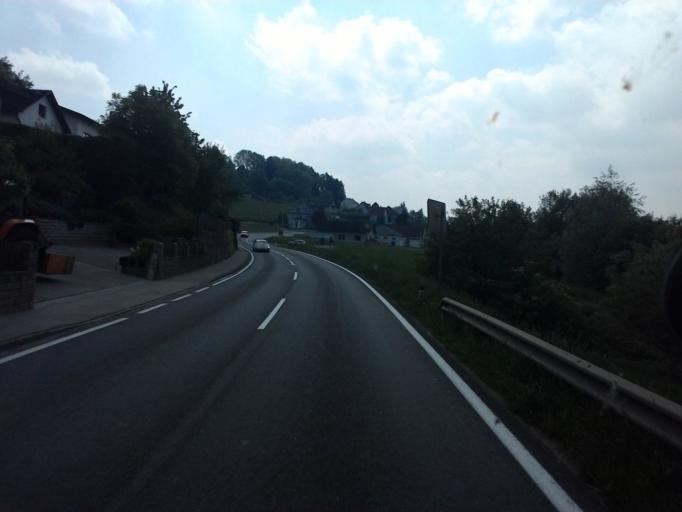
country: AT
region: Upper Austria
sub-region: Politischer Bezirk Kirchdorf an der Krems
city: Kremsmunster
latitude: 48.0514
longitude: 14.1374
